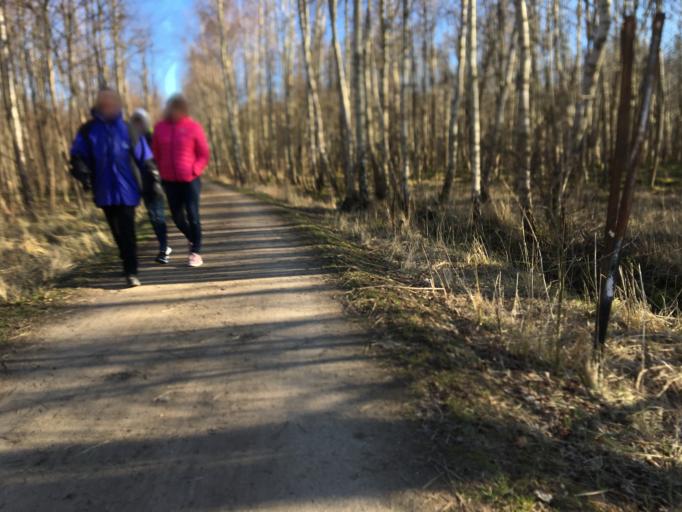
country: DK
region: Capital Region
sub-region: Tarnby Kommune
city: Tarnby
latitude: 55.5950
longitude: 12.5540
